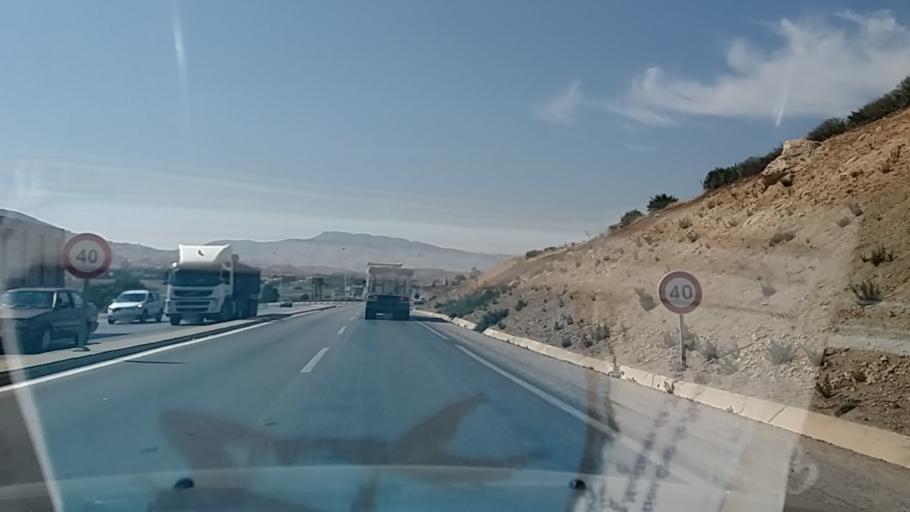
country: MA
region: Tanger-Tetouan
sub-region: Tetouan
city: Saddina
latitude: 35.5578
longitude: -5.4523
